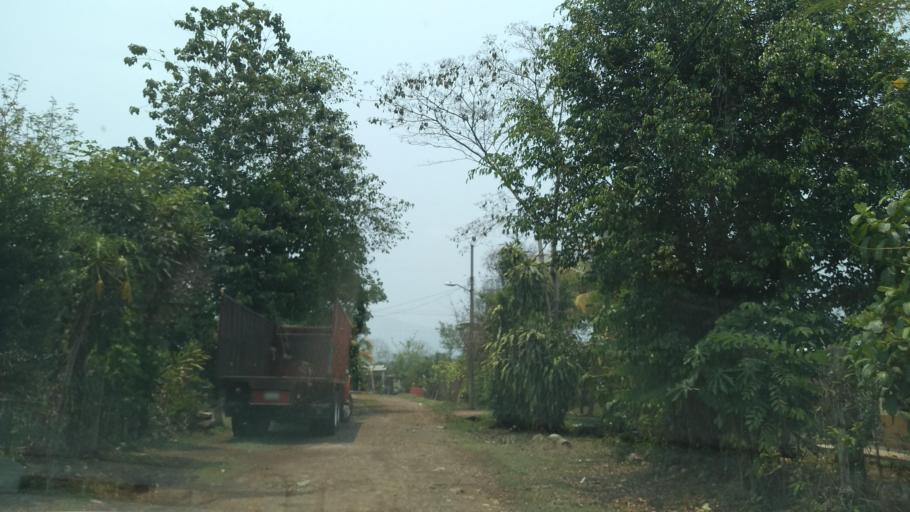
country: MX
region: Veracruz
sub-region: Tezonapa
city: Laguna Chica (Pueblo Nuevo)
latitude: 18.5157
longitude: -96.7361
